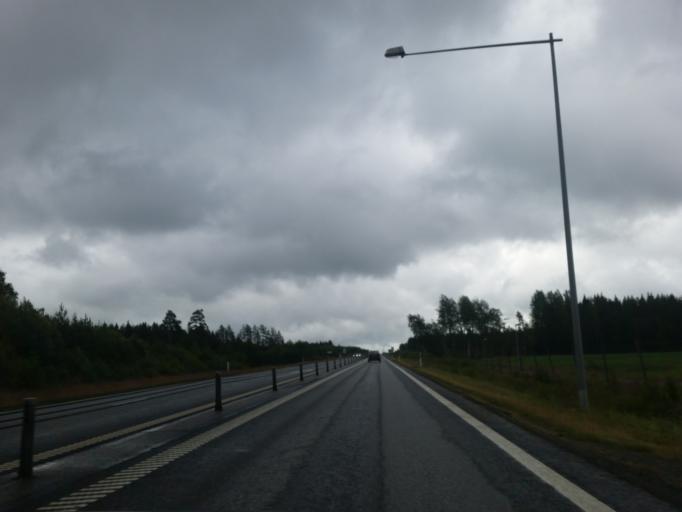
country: SE
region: Vaesterbotten
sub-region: Umea Kommun
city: Ersmark
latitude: 63.8572
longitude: 20.3942
